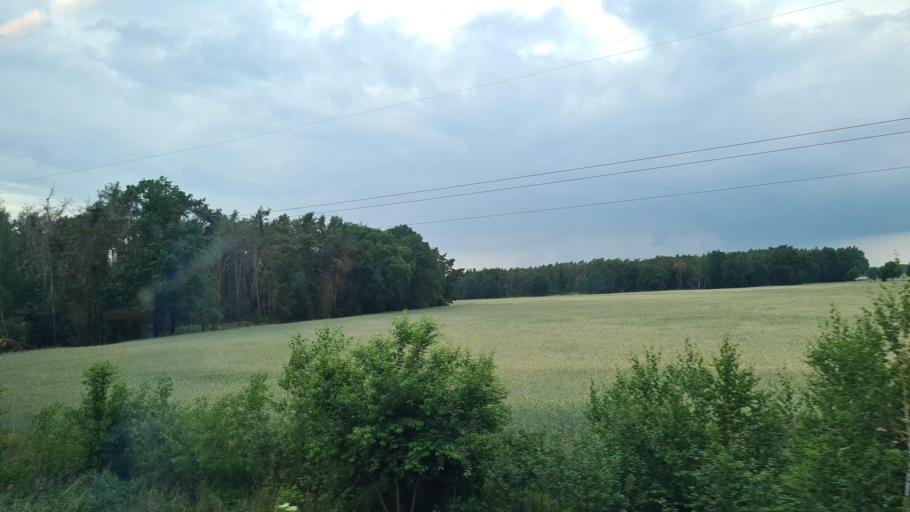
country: DE
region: Brandenburg
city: Schilda
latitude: 51.5872
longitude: 13.3197
